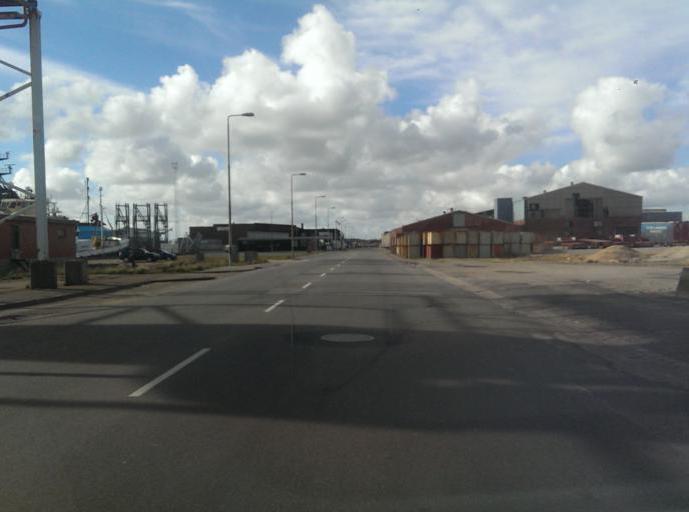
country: DK
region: South Denmark
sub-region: Esbjerg Kommune
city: Esbjerg
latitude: 55.4783
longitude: 8.4226
